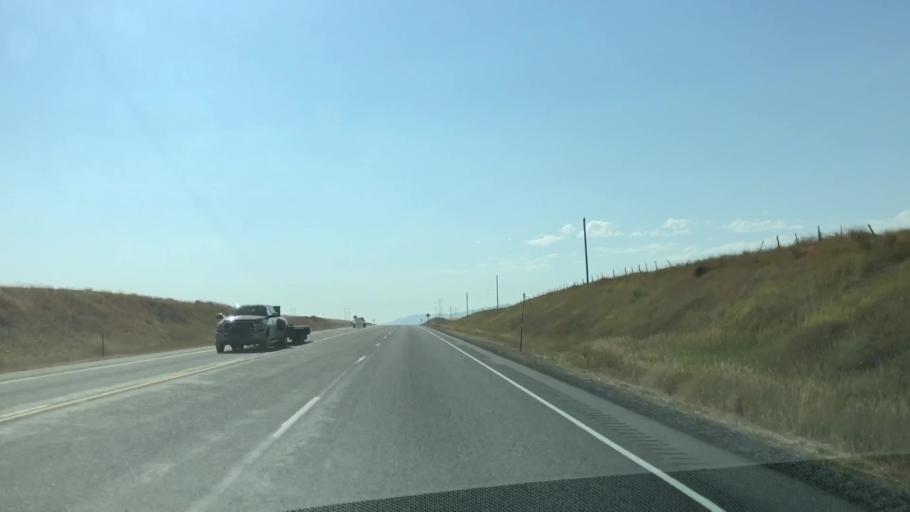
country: US
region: Idaho
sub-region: Teton County
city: Victor
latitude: 43.5294
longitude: -111.5029
